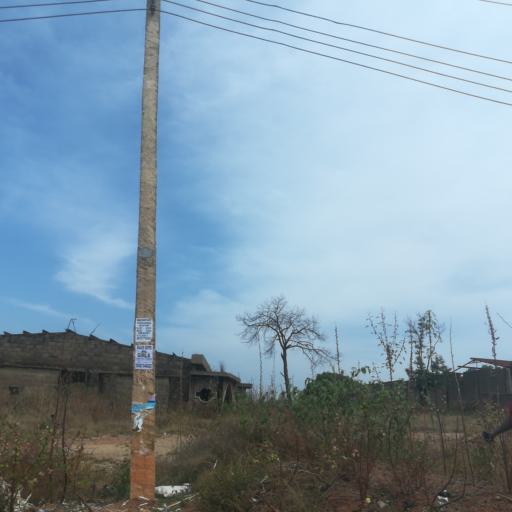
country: NG
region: Plateau
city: Jos
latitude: 9.8782
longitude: 8.8715
